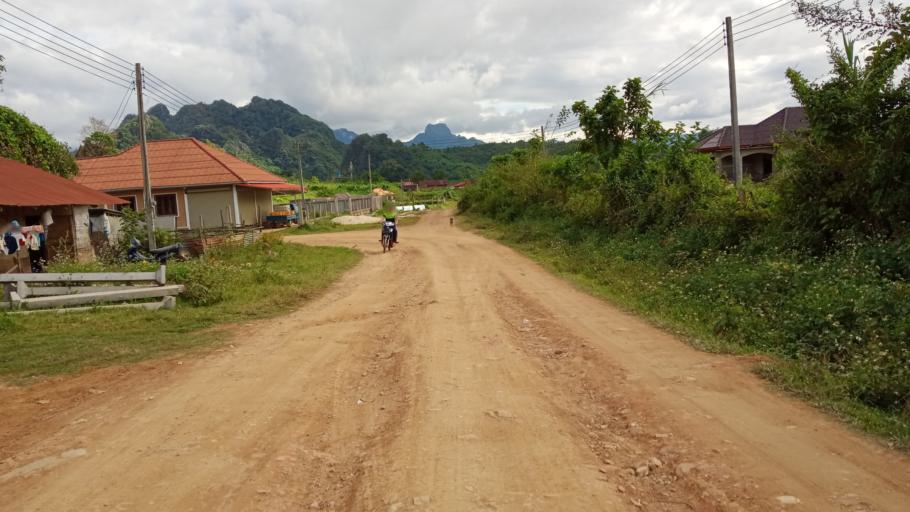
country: LA
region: Xiangkhoang
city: Phonsavan
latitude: 19.1079
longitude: 102.9269
